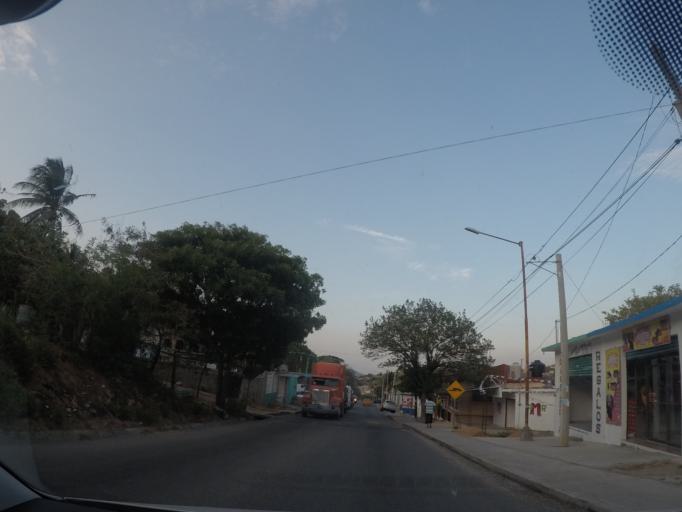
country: MX
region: Oaxaca
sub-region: Salina Cruz
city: Salina Cruz
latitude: 16.1925
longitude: -95.2073
